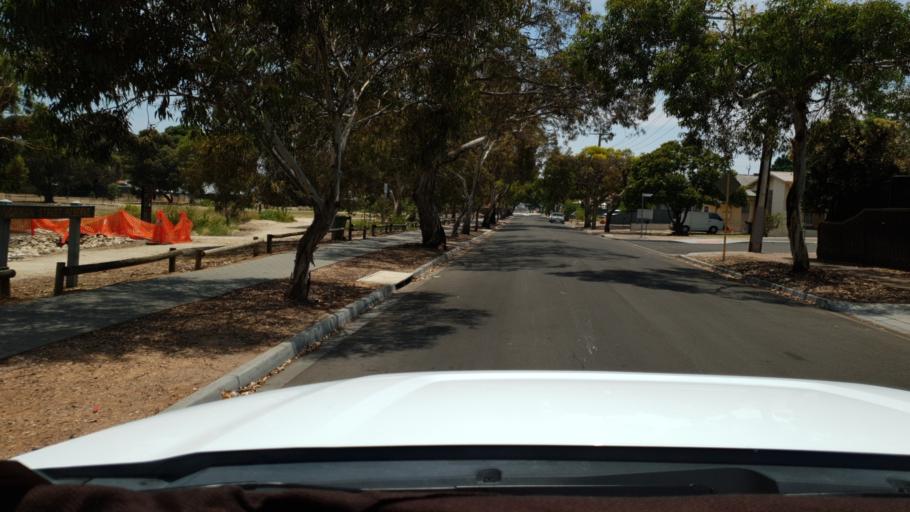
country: AU
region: South Australia
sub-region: Marion
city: Clovelly Park
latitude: -35.0079
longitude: 138.5813
